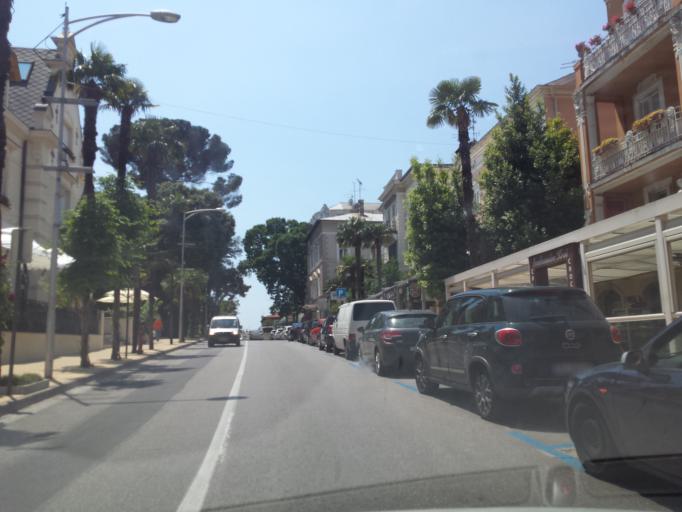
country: HR
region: Primorsko-Goranska
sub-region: Grad Opatija
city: Opatija
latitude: 45.3375
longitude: 14.3083
